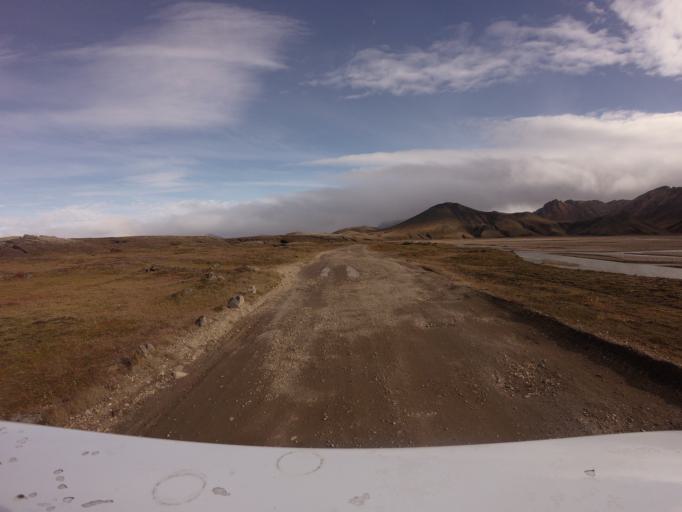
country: IS
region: South
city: Vestmannaeyjar
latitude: 64.0035
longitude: -19.0256
